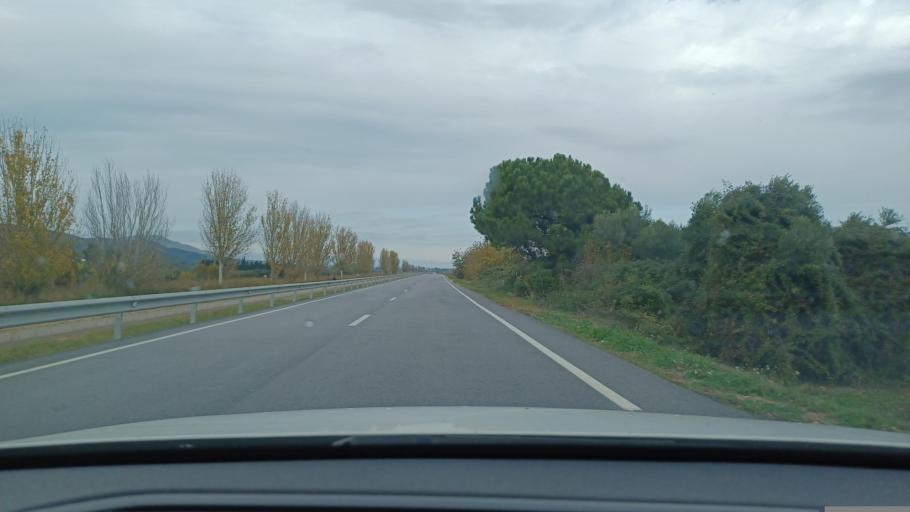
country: ES
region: Catalonia
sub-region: Provincia de Tarragona
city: Sant Carles de la Rapita
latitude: 40.6476
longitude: 0.5981
